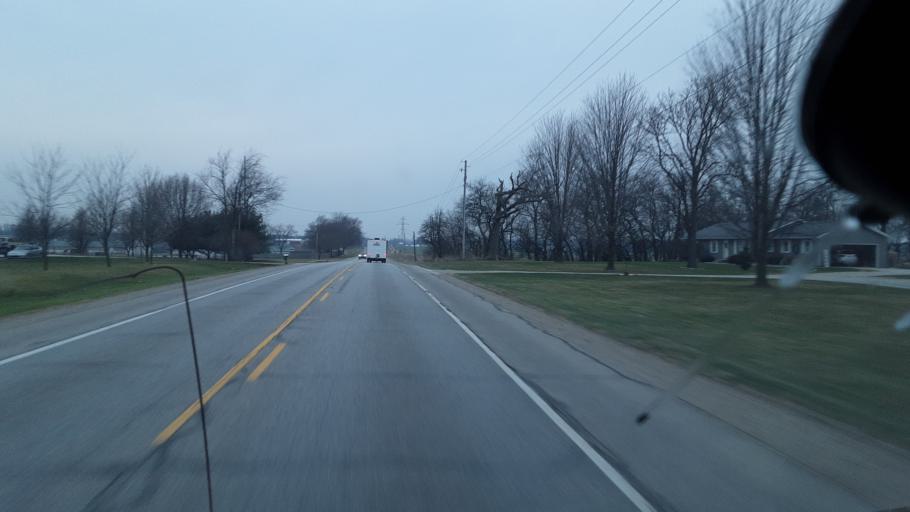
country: US
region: Indiana
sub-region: Elkhart County
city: Middlebury
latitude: 41.6678
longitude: -85.7592
